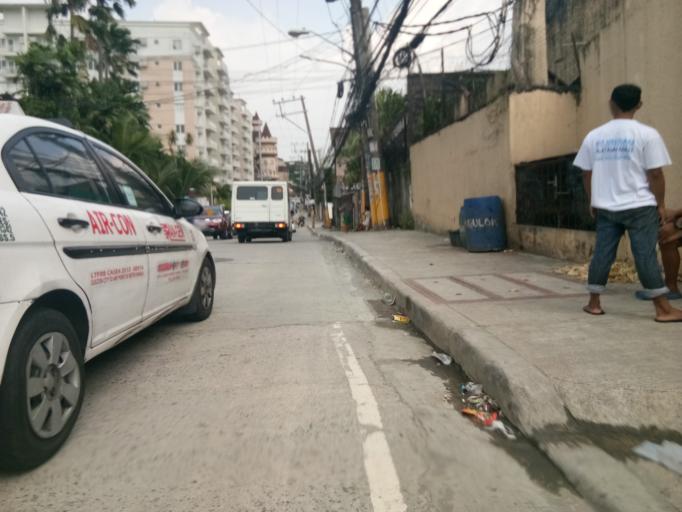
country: PH
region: Metro Manila
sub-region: San Juan
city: San Juan
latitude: 14.6135
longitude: 121.0465
